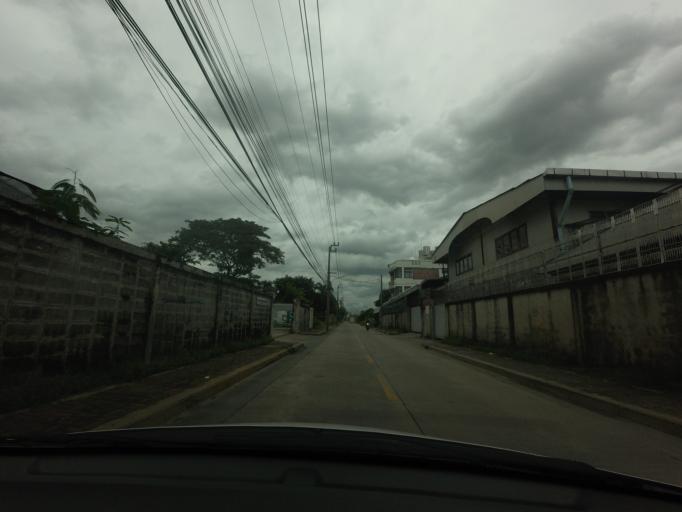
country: TH
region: Bangkok
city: Min Buri
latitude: 13.7922
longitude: 100.7478
